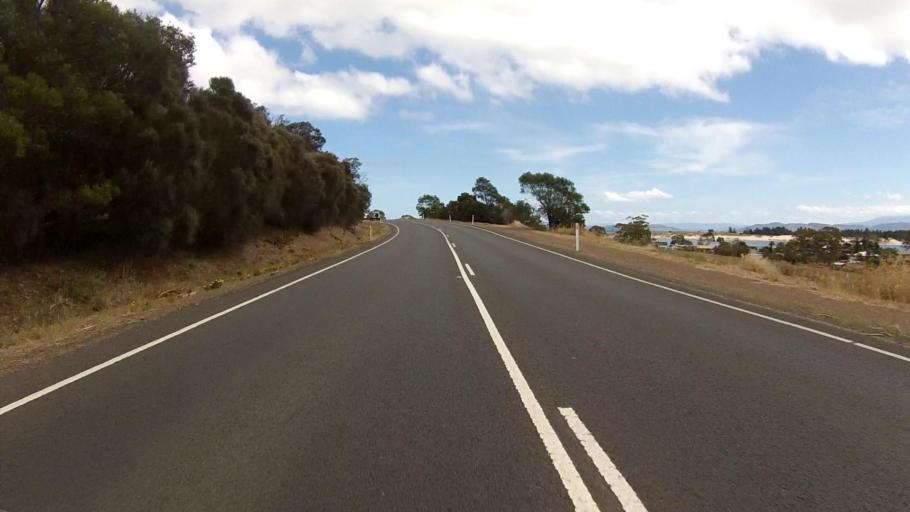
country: AU
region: Tasmania
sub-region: Sorell
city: Sorell
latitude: -42.8369
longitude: 147.6235
